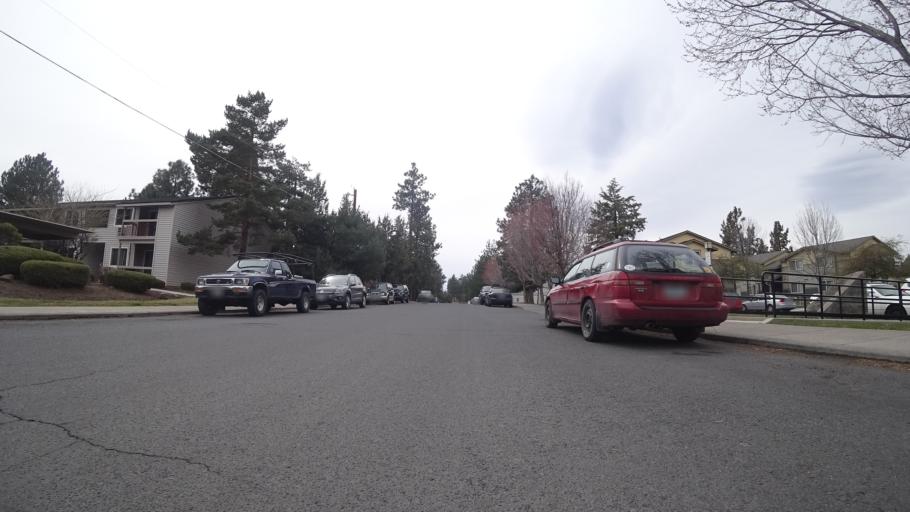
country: US
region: Oregon
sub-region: Deschutes County
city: Bend
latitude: 44.0460
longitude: -121.2803
